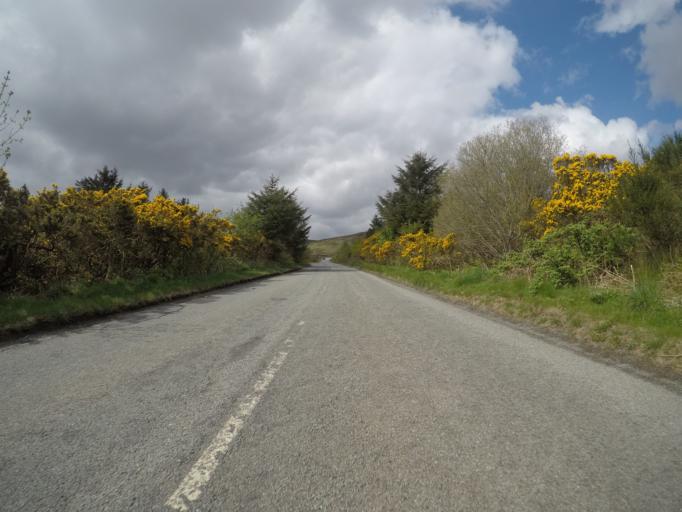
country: GB
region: Scotland
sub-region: Highland
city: Isle of Skye
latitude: 57.3011
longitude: -6.2962
